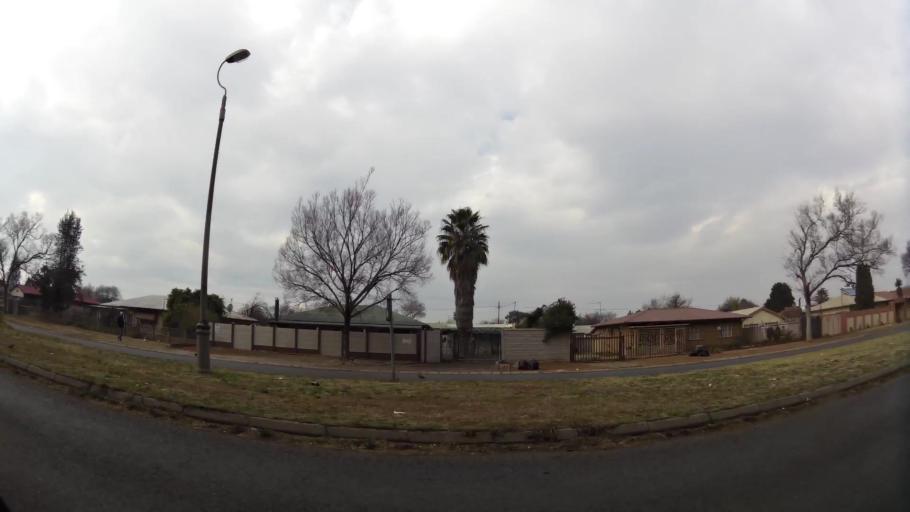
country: ZA
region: Gauteng
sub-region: Sedibeng District Municipality
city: Vanderbijlpark
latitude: -26.6872
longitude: 27.8267
